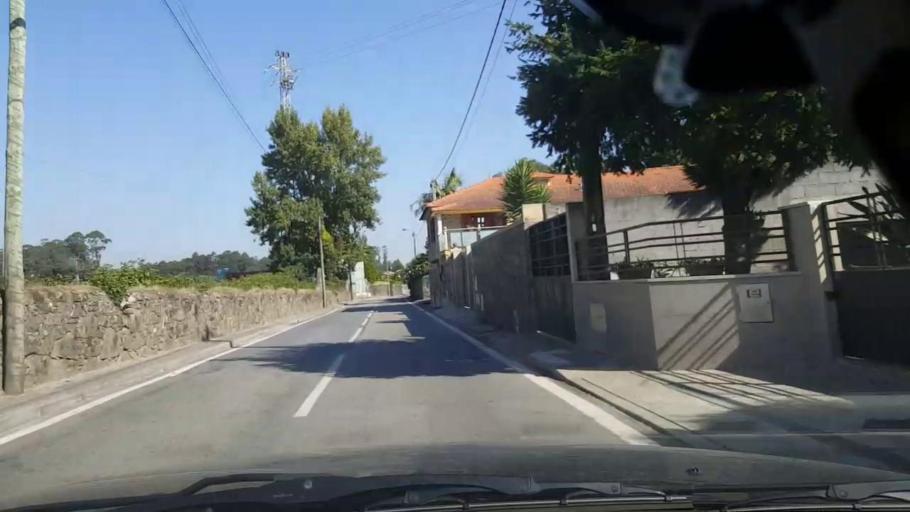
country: PT
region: Porto
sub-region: Vila do Conde
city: Arvore
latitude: 41.3125
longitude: -8.6792
